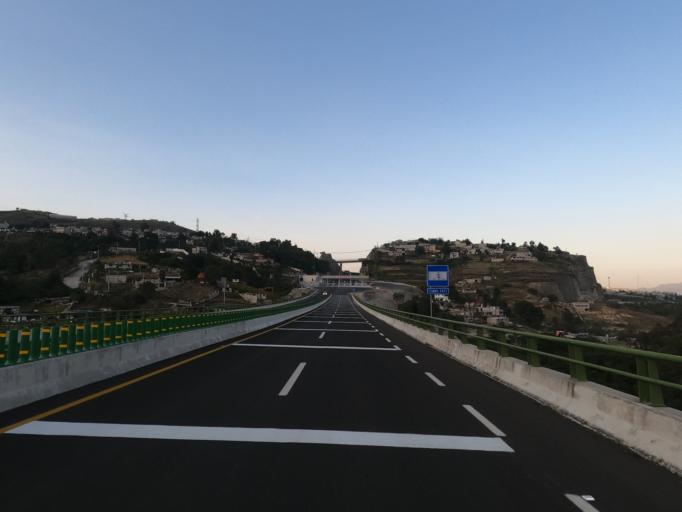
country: MX
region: Mexico
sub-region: Naucalpan de Juarez
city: Ejido el Castillo
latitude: 19.4308
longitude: -99.3043
